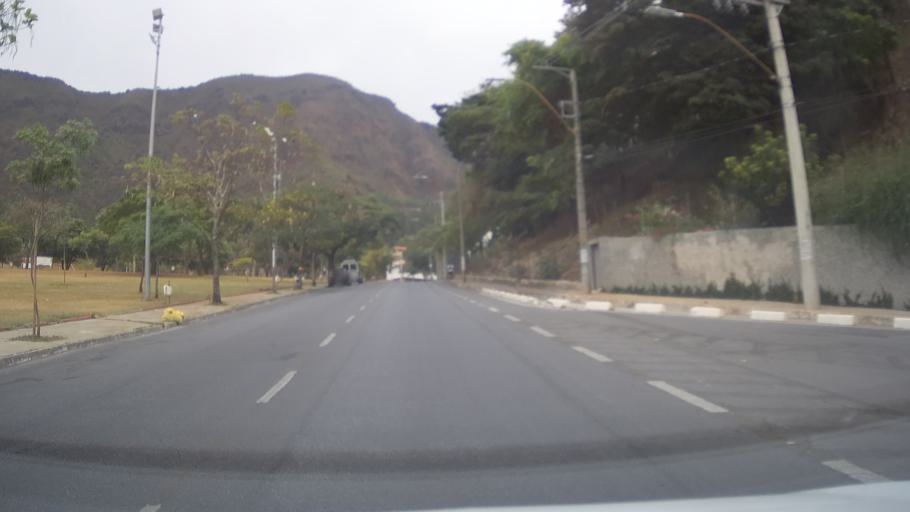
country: BR
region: Minas Gerais
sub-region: Belo Horizonte
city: Belo Horizonte
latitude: -19.9560
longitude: -43.9155
